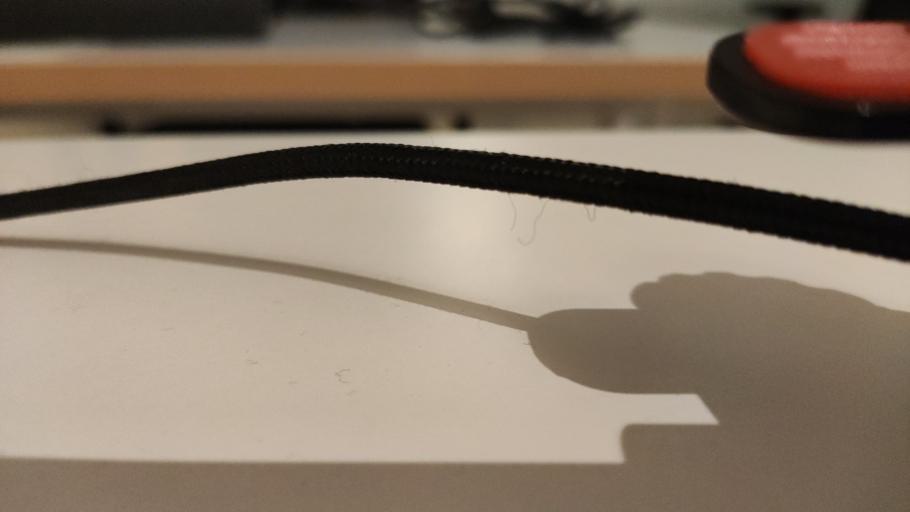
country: RU
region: Moskovskaya
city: Semkhoz
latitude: 56.3995
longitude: 38.0319
